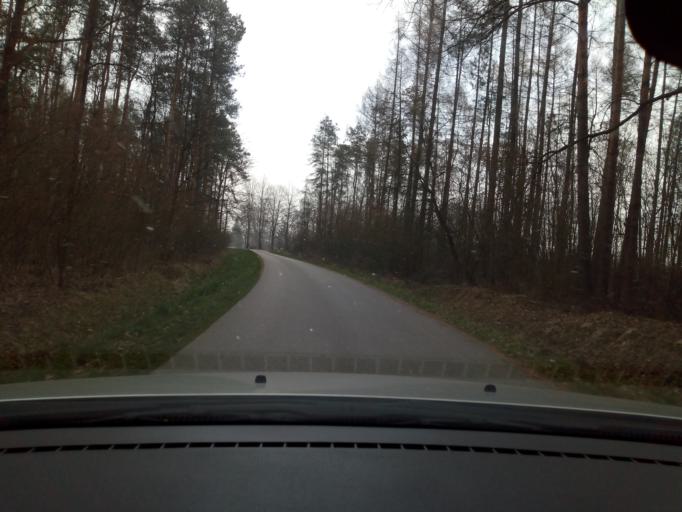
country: PL
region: Masovian Voivodeship
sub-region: Powiat lipski
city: Rzeczniow
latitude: 51.0827
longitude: 21.3469
